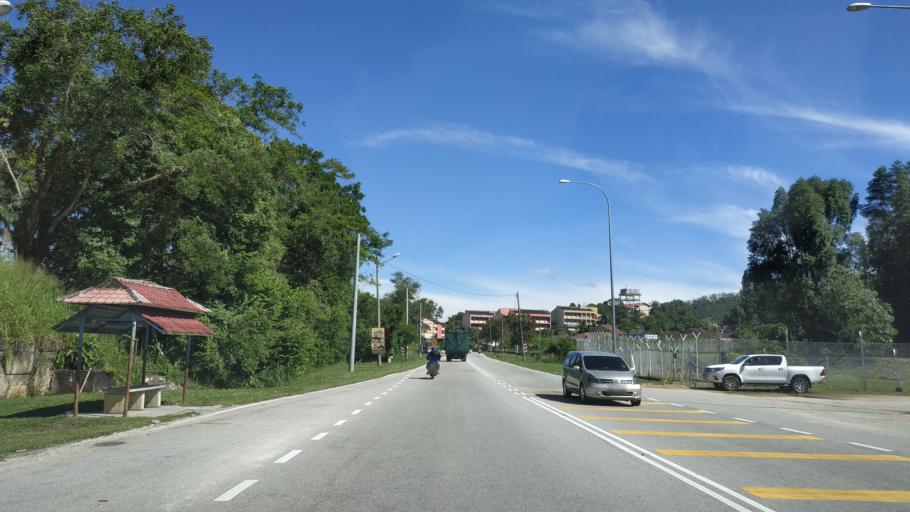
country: MY
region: Kedah
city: Kulim
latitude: 5.3356
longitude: 100.5372
